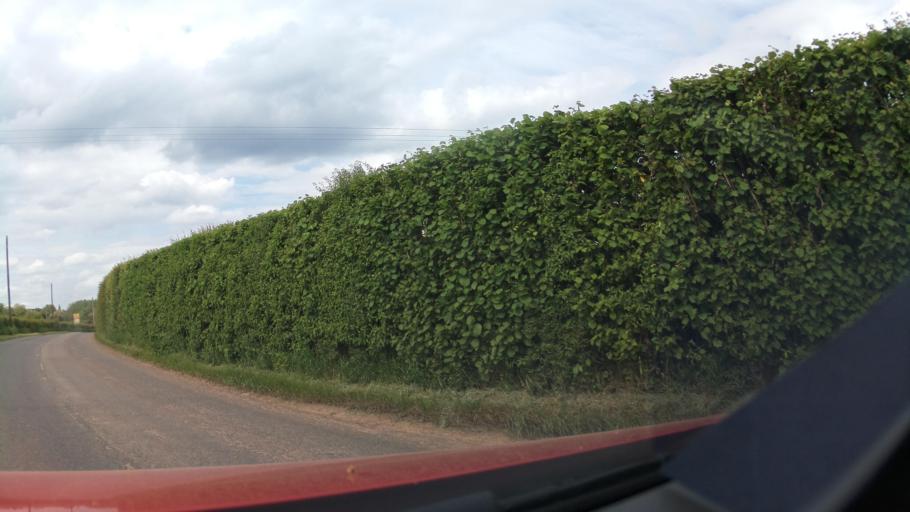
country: GB
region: England
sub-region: Herefordshire
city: Ledbury
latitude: 52.0585
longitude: -2.4429
